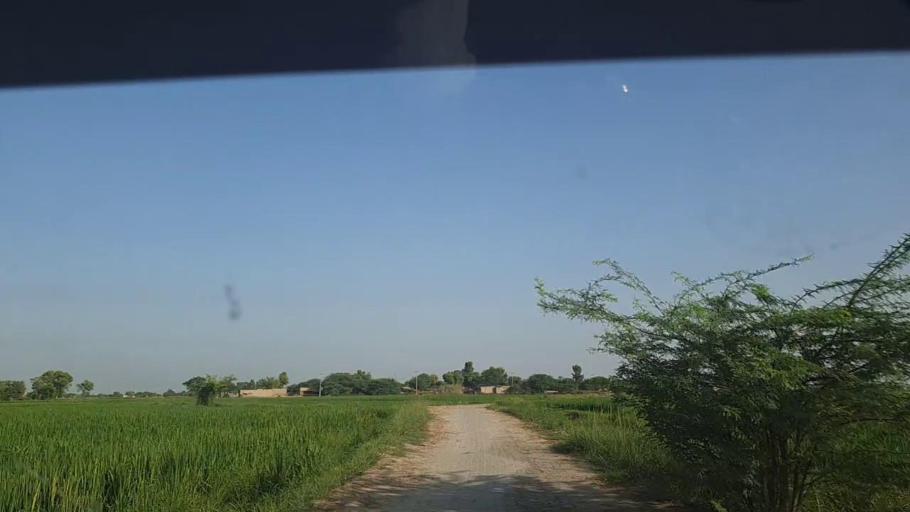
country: PK
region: Sindh
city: Tangwani
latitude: 28.2686
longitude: 69.0112
